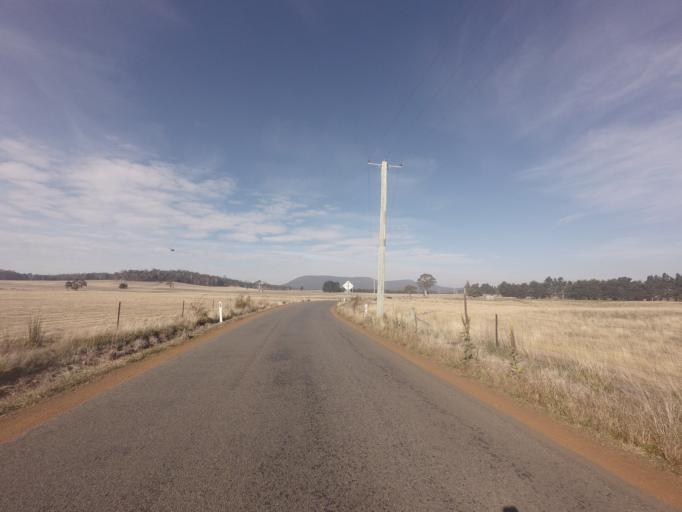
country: AU
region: Tasmania
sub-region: Sorell
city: Sorell
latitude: -42.4314
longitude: 147.4699
